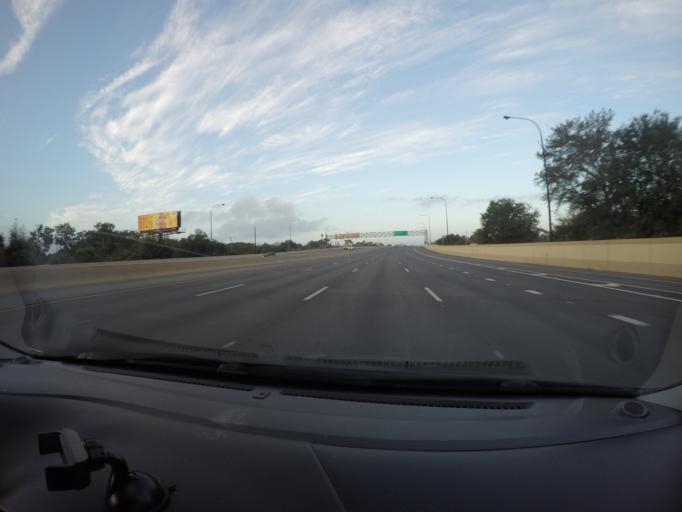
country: US
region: Florida
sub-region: Orange County
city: Azalea Park
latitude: 28.5401
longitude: -81.2885
